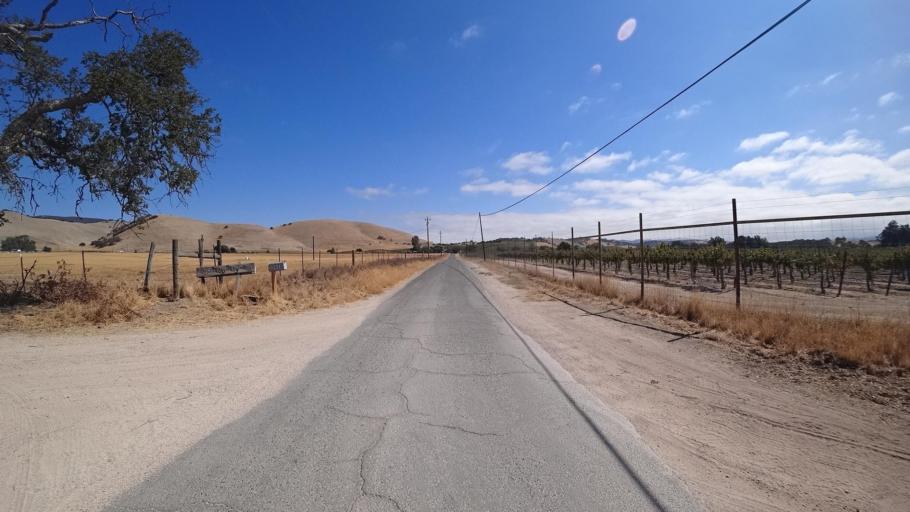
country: US
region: California
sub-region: San Luis Obispo County
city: Lake Nacimiento
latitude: 35.9090
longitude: -121.0283
